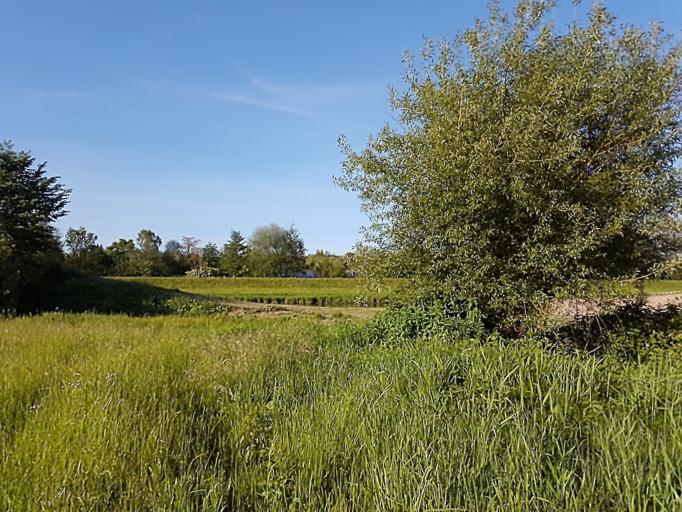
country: DE
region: Baden-Wuerttemberg
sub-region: Freiburg Region
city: Teningen
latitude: 48.1370
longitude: 7.7943
